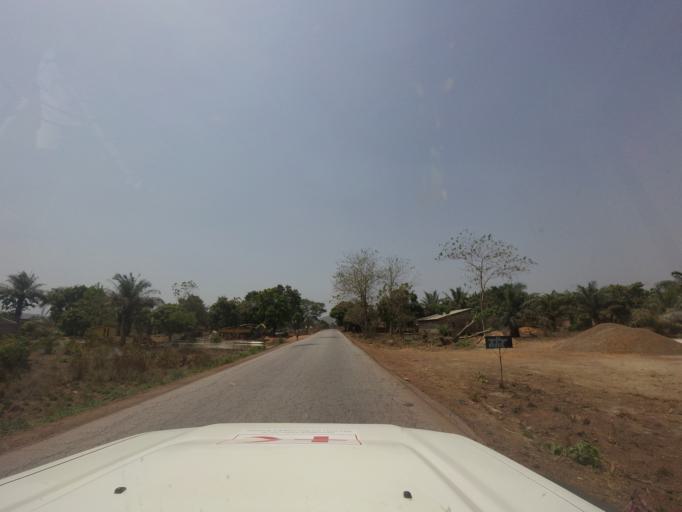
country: GN
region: Kindia
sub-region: Kindia
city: Kindia
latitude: 9.8744
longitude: -13.0534
